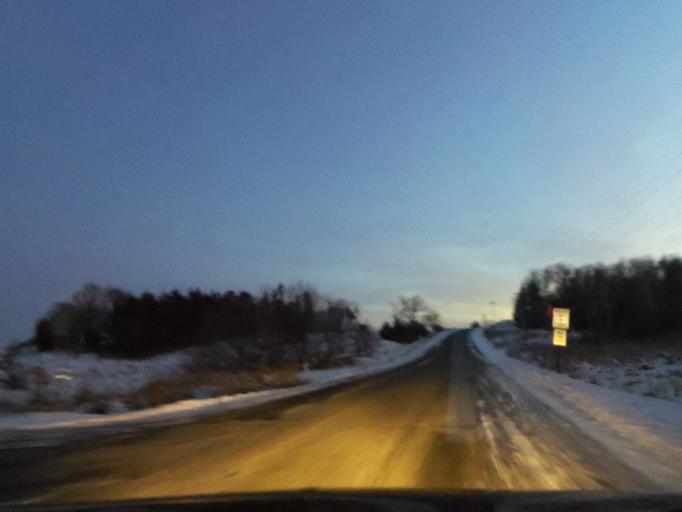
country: US
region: Minnesota
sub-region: Chisago County
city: Shafer
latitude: 45.3656
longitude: -92.7795
